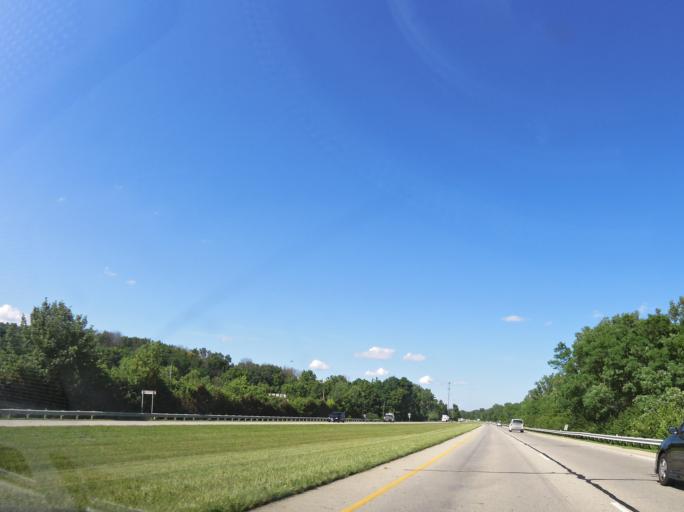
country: US
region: Ohio
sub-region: Greene County
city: Wright-Patterson AFB
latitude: 39.8194
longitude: -84.0725
